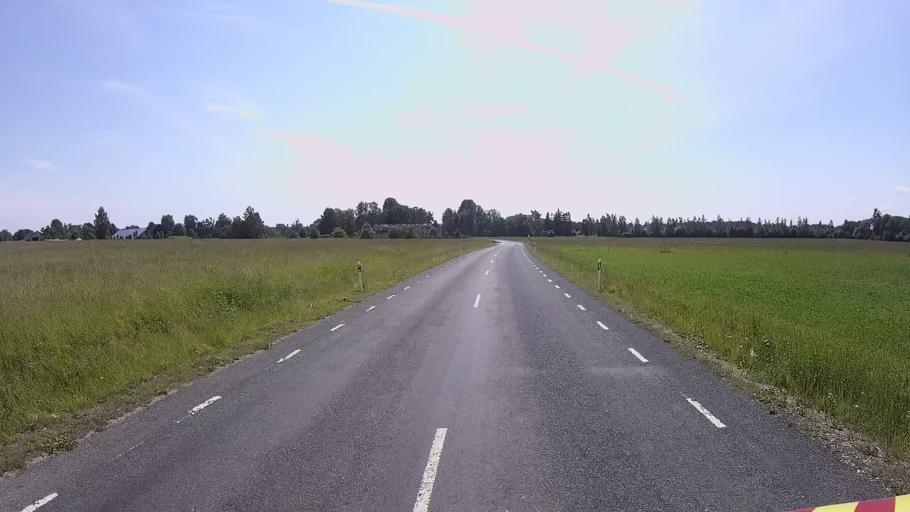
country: EE
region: Viljandimaa
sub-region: Karksi vald
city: Karksi-Nuia
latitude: 58.0680
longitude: 25.5524
